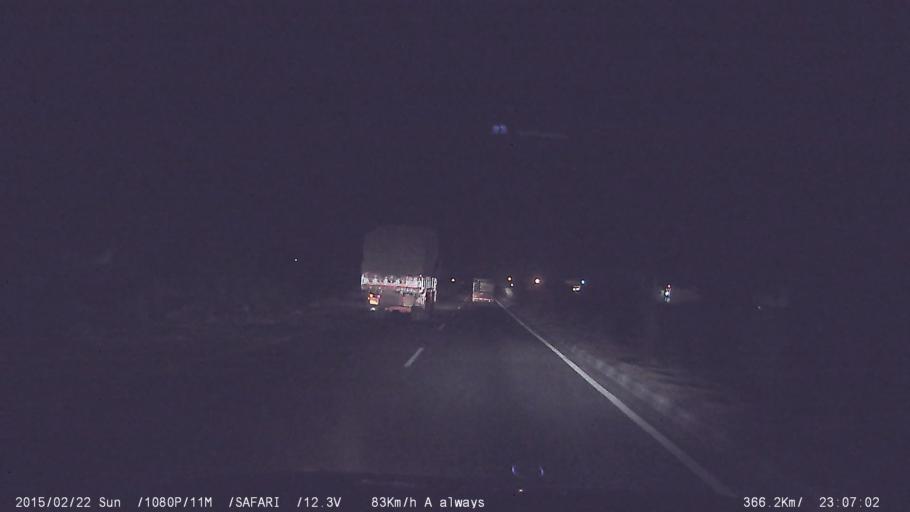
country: IN
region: Tamil Nadu
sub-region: Namakkal
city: Rasipuram
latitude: 11.4359
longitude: 78.1568
